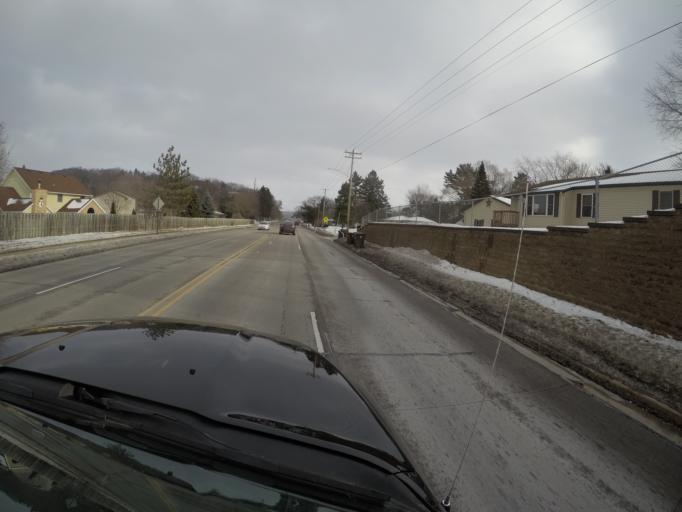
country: US
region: Wisconsin
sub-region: La Crosse County
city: Onalaska
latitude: 43.8805
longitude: -91.2073
